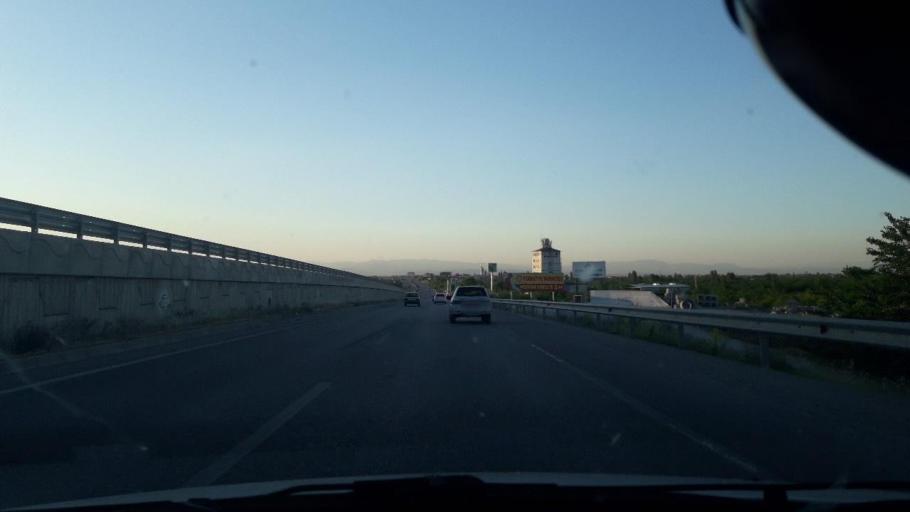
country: TR
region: Malatya
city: Yesilyurt
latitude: 38.3412
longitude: 38.2344
